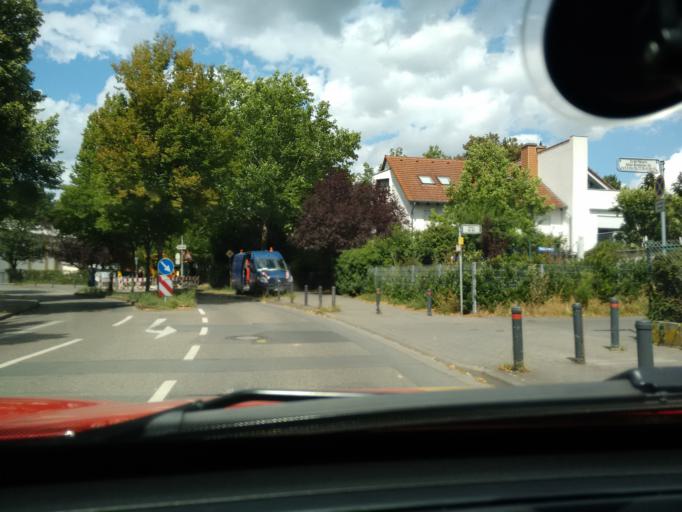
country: DE
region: Rheinland-Pfalz
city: Mainz
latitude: 49.9848
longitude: 8.2540
